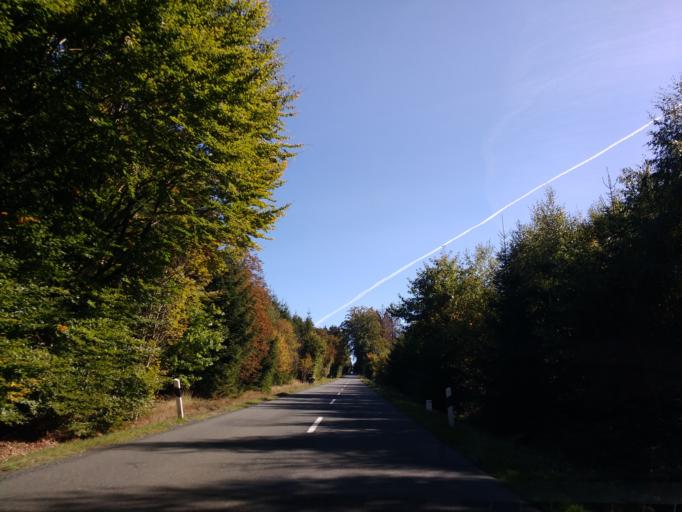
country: DE
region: North Rhine-Westphalia
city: Lichtenau
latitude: 51.6215
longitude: 8.9634
